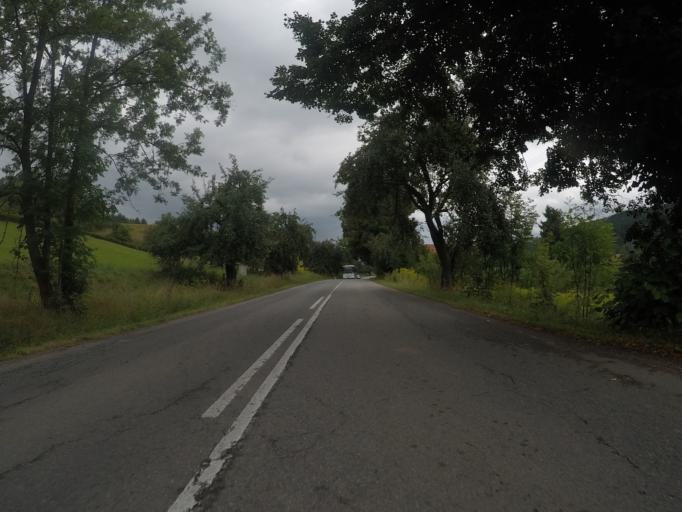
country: SK
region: Kosicky
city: Spisska Nova Ves
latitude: 48.9186
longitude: 20.5358
